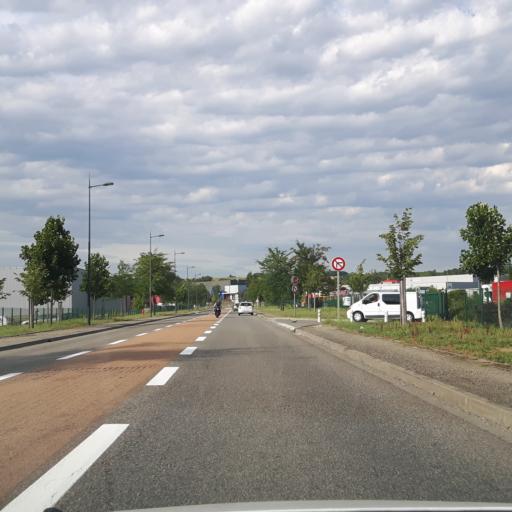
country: FR
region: Midi-Pyrenees
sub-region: Departement de la Haute-Garonne
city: Castelnau-d'Estretefonds
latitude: 43.7659
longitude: 1.3759
